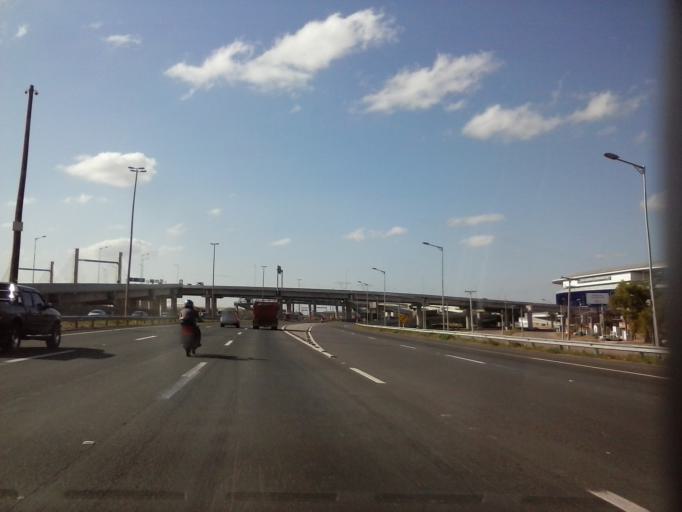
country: BR
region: Rio Grande do Sul
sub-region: Canoas
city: Canoas
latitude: -29.9772
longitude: -51.1998
